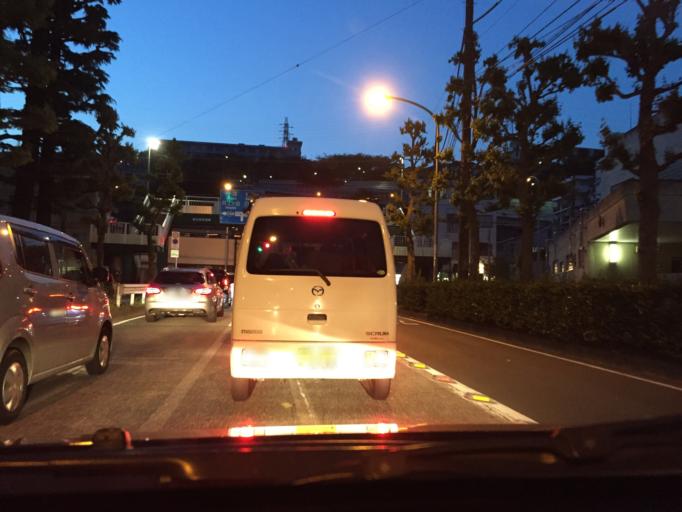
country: JP
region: Kanagawa
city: Yokohama
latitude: 35.4352
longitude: 139.6107
